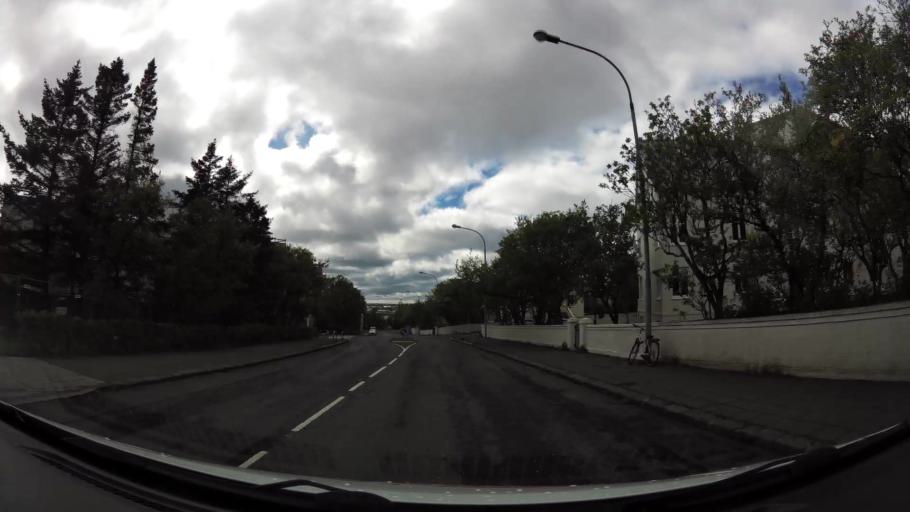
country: IS
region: Capital Region
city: Kopavogur
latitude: 64.1395
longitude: -21.9289
